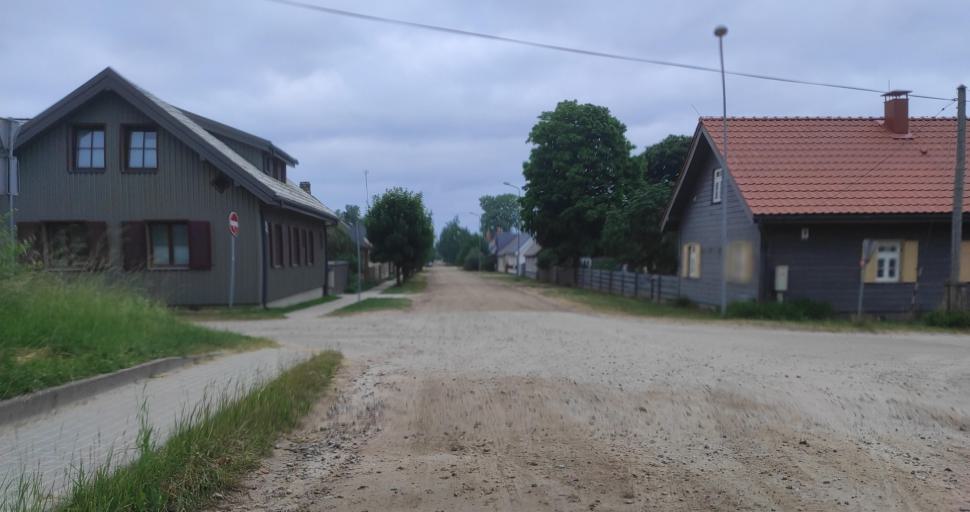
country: LV
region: Pavilostas
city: Pavilosta
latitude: 56.8894
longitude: 21.1842
